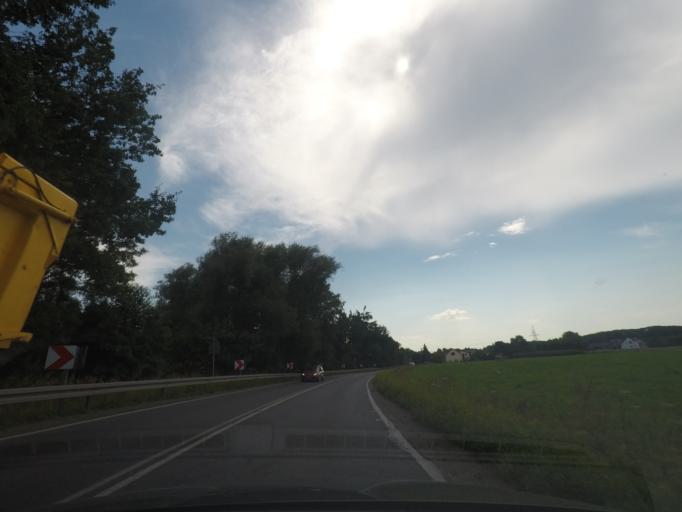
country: PL
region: Lesser Poland Voivodeship
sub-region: Powiat oswiecimski
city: Przecieszyn
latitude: 49.9962
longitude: 19.1726
